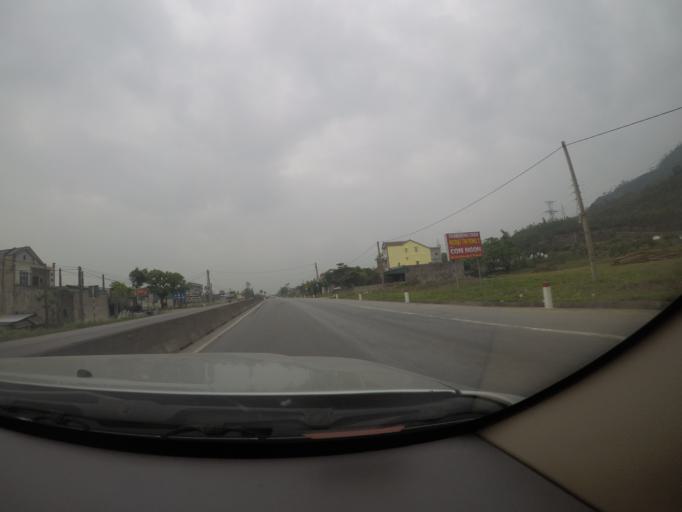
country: VN
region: Ha Tinh
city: Ky Anh
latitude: 18.1318
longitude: 106.2552
